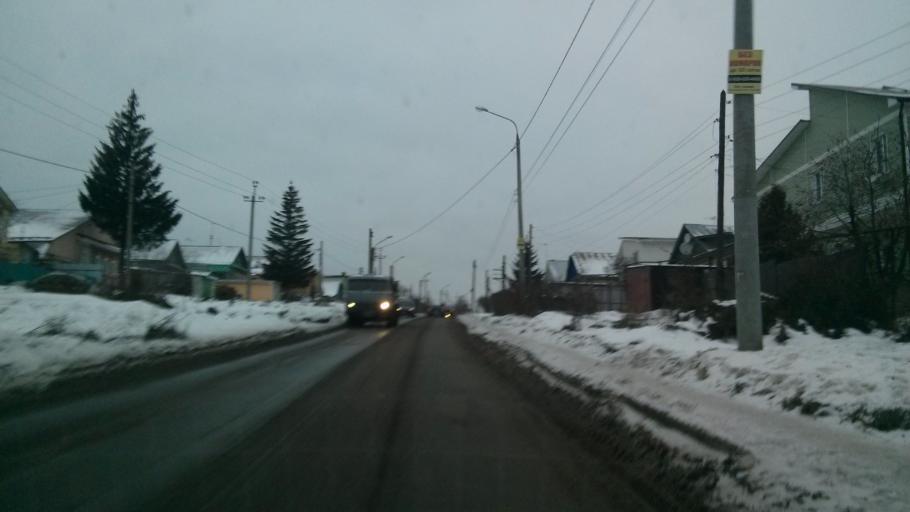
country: RU
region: Nizjnij Novgorod
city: Afonino
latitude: 56.2954
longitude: 44.0892
